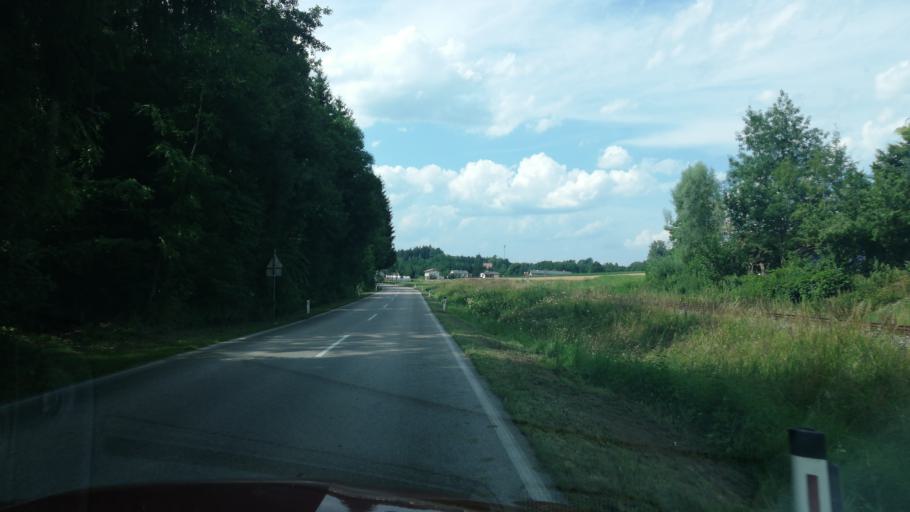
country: AT
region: Upper Austria
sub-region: Politischer Bezirk Vocklabruck
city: Puhret
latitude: 48.0314
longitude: 13.7038
